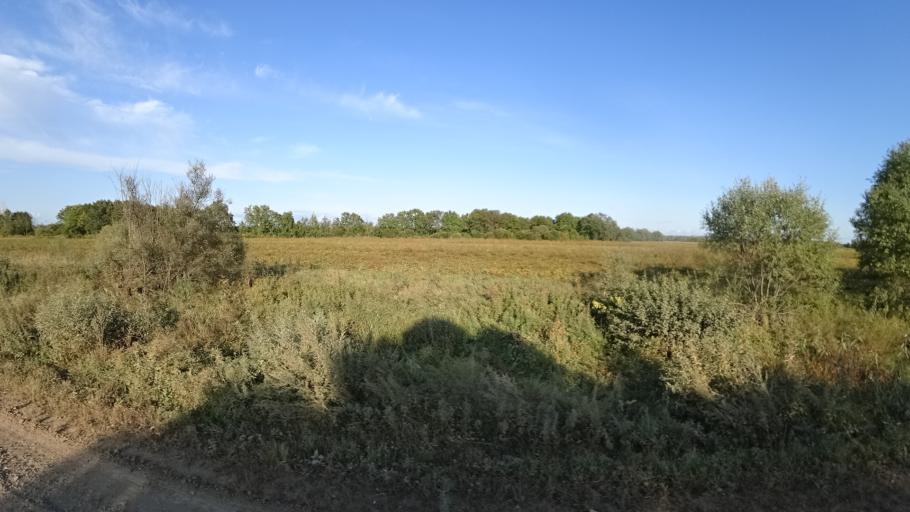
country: RU
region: Amur
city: Arkhara
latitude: 49.3581
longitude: 130.1372
